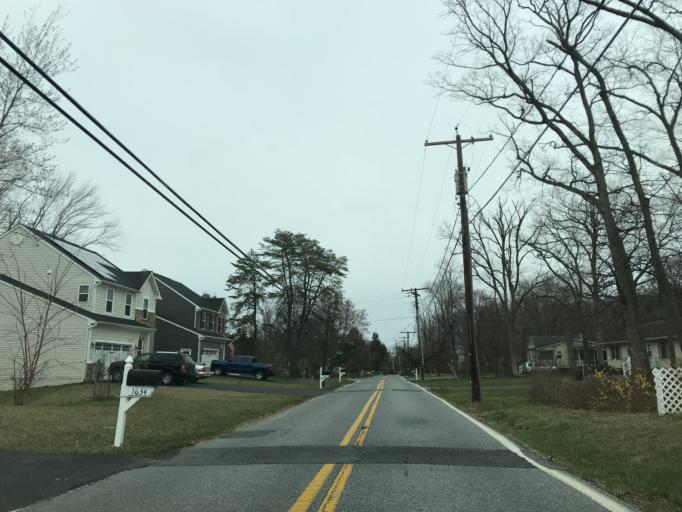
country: US
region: Maryland
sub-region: Baltimore County
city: Middle River
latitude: 39.2968
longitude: -76.4288
